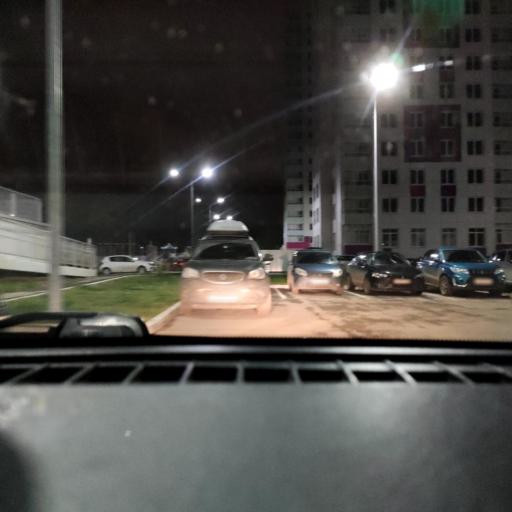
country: RU
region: Perm
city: Perm
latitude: 57.9897
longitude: 56.2649
